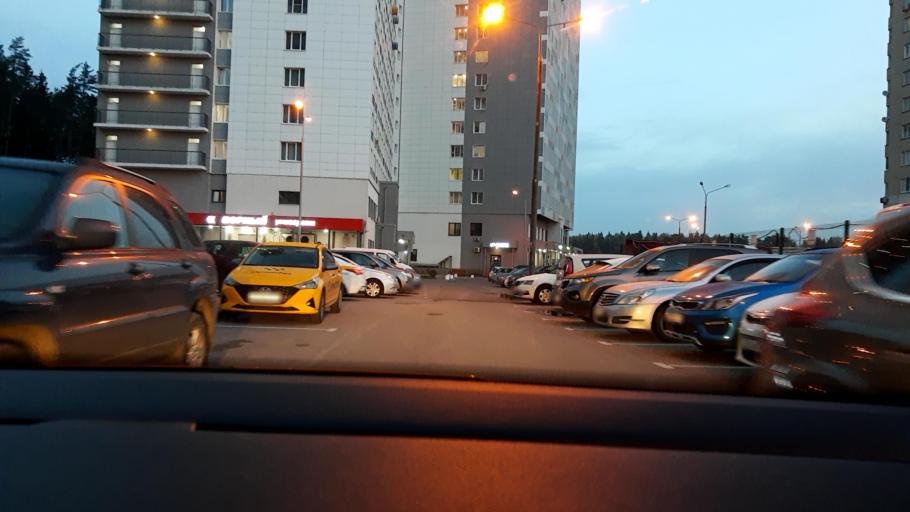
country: RU
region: Moscow
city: Vostochnyy
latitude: 55.8229
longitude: 37.8886
